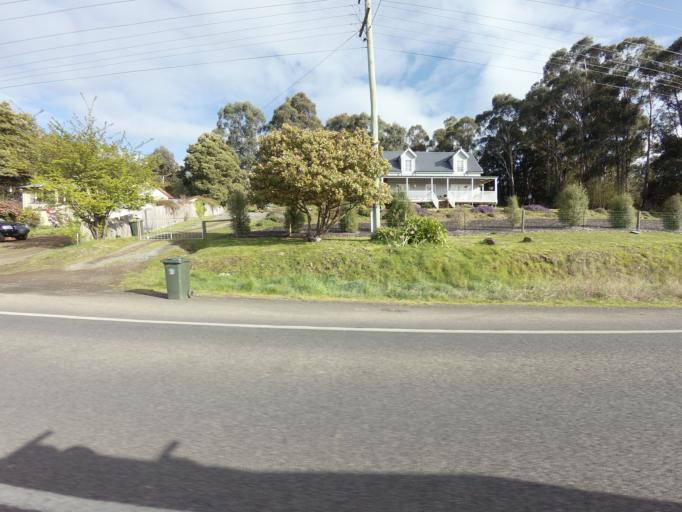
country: AU
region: Tasmania
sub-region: Huon Valley
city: Franklin
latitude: -43.0621
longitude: 147.0271
